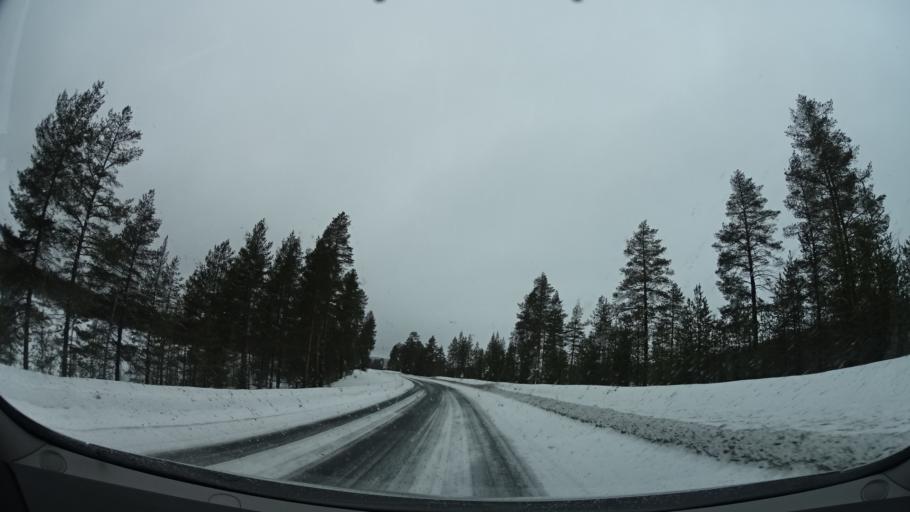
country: SE
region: Vaesterbotten
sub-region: Mala Kommun
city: Mala
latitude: 65.1444
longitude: 18.8310
